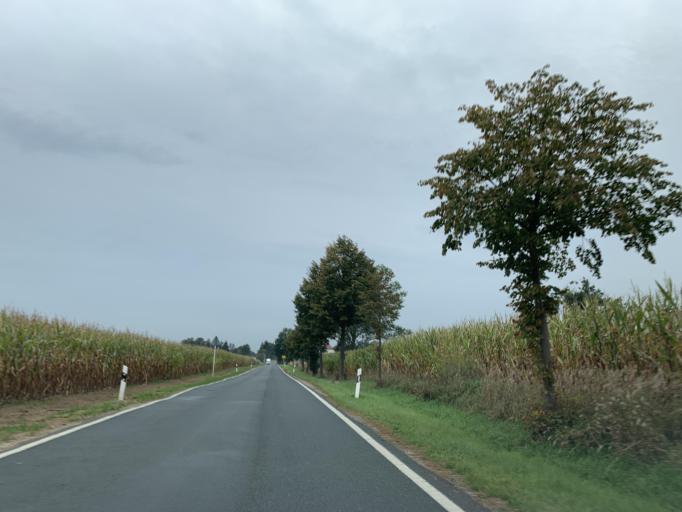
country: DE
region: Mecklenburg-Vorpommern
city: Woldegk
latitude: 53.3277
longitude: 13.5887
